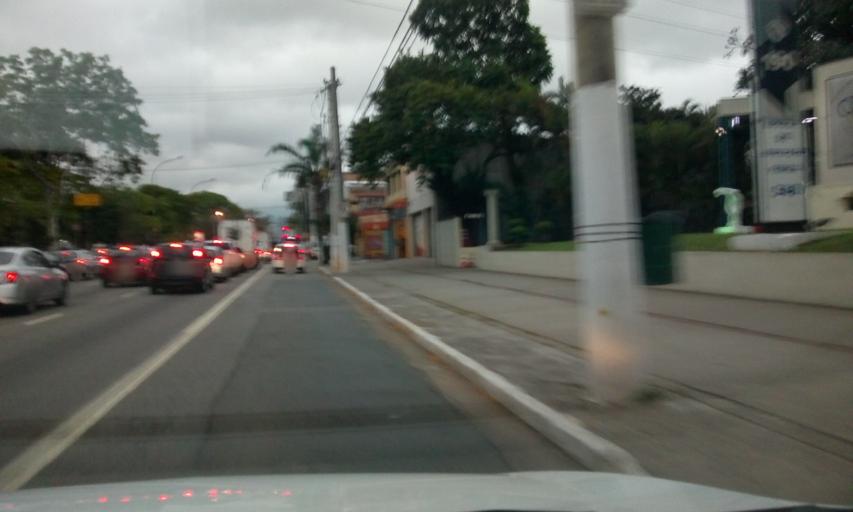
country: BR
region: Sao Paulo
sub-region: Sao Paulo
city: Sao Paulo
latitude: -23.5270
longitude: -46.6253
